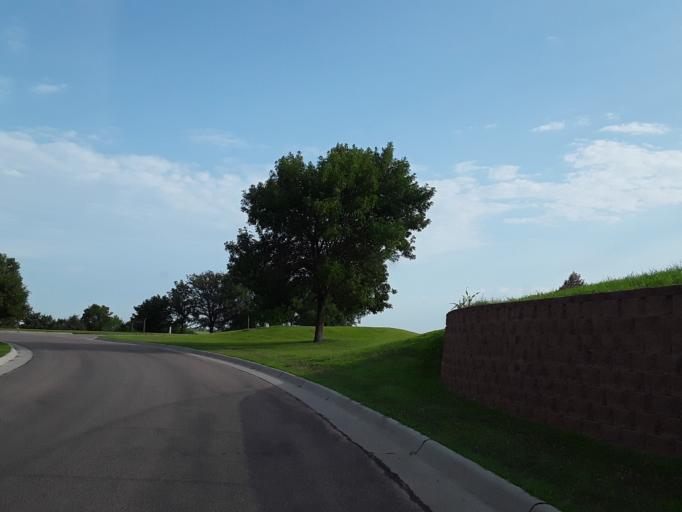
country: US
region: Nebraska
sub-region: Saunders County
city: Ashland
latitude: 41.0261
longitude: -96.3096
